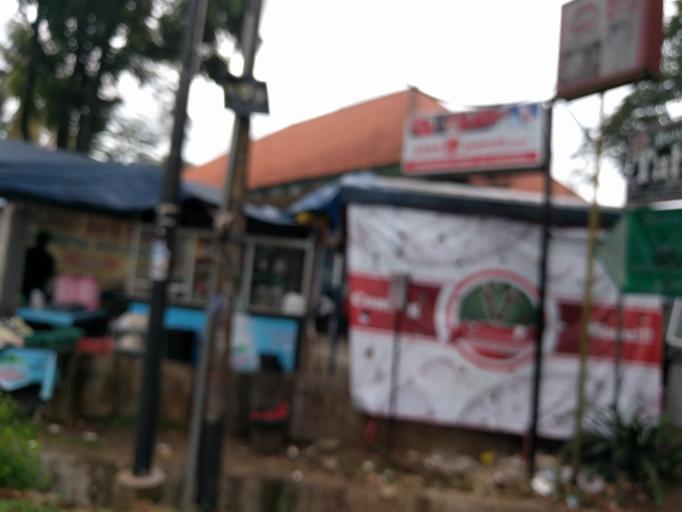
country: ID
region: West Java
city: Bogor
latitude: -6.5914
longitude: 106.8058
